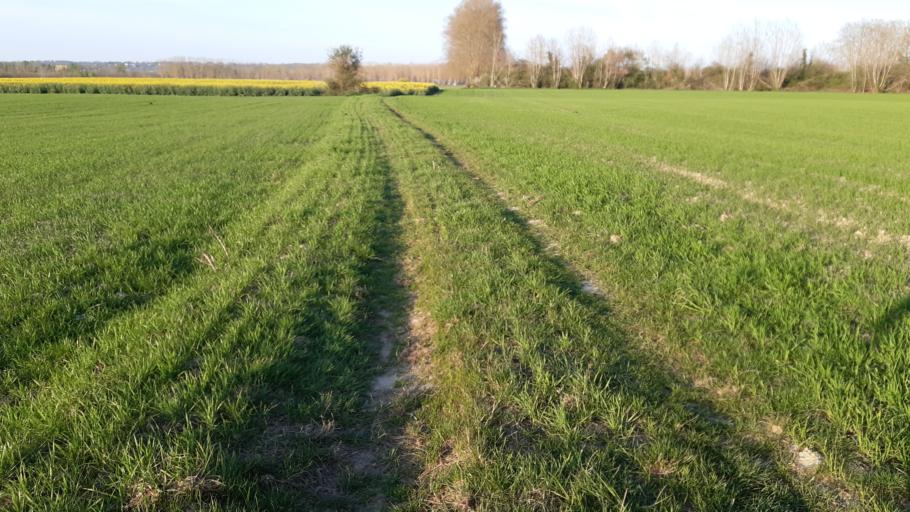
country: FR
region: Midi-Pyrenees
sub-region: Departement de la Haute-Garonne
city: Ondes
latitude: 43.7647
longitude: 1.3099
